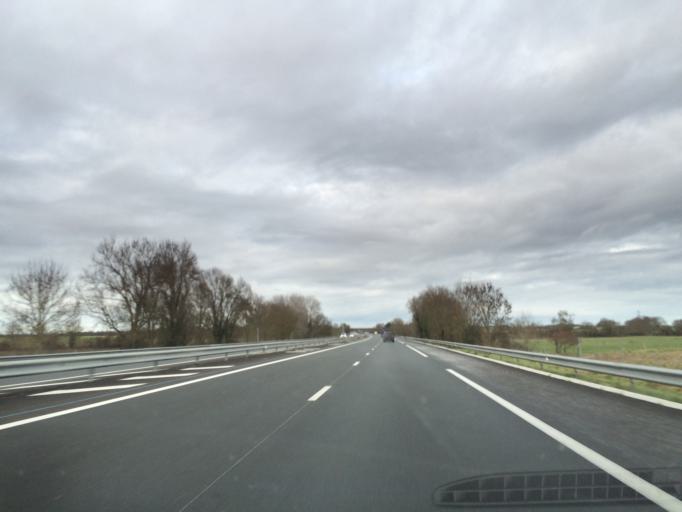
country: FR
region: Poitou-Charentes
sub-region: Departement des Deux-Sevres
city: Beauvoir-sur-Niort
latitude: 46.1531
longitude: -0.5186
